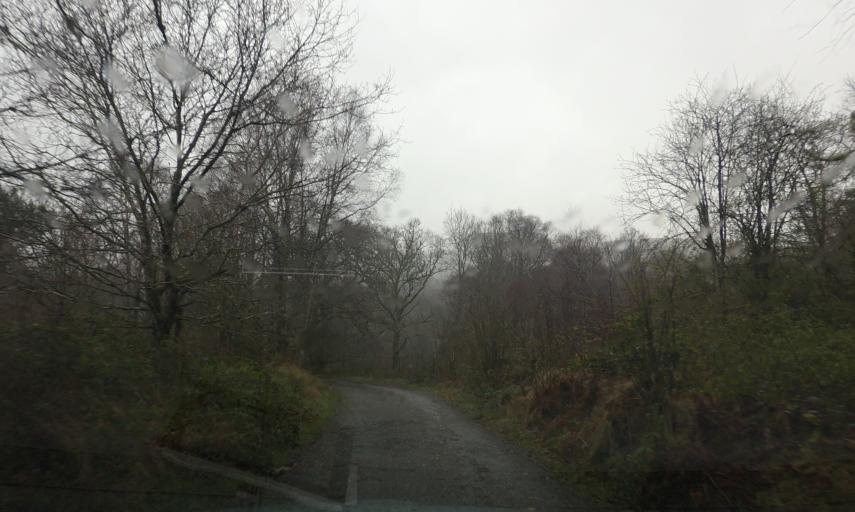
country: GB
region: Scotland
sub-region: West Dunbartonshire
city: Balloch
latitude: 56.1578
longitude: -4.6414
